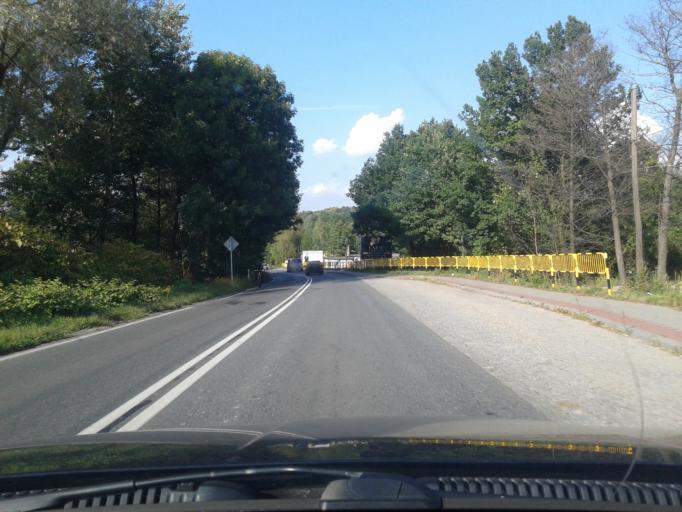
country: PL
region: Silesian Voivodeship
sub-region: Powiat wodzislawski
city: Turza Slaska
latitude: 49.9857
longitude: 18.4542
